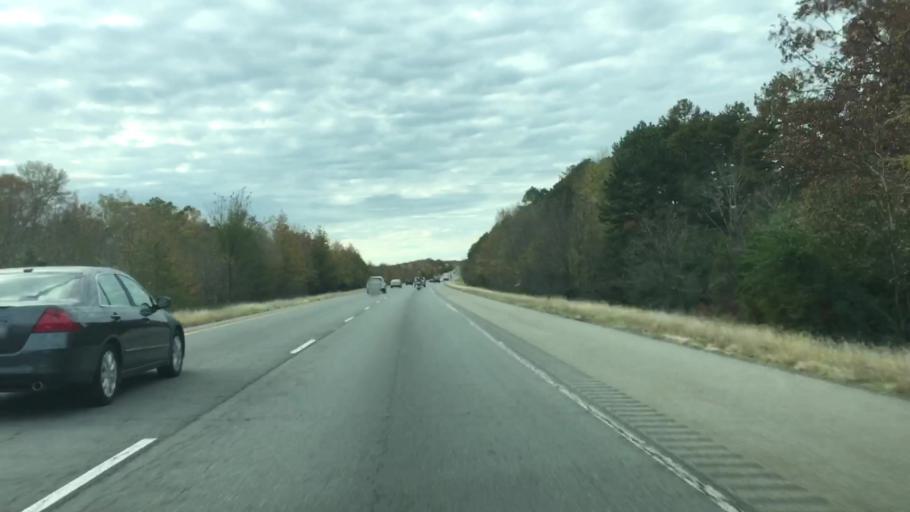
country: US
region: Arkansas
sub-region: Faulkner County
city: Conway
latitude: 35.1208
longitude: -92.4854
